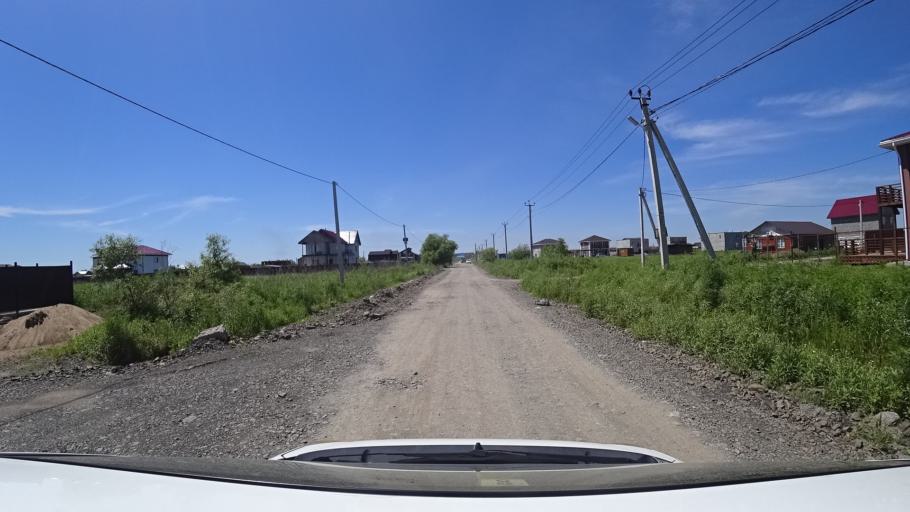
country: RU
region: Khabarovsk Krai
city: Topolevo
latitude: 48.5151
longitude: 135.1936
